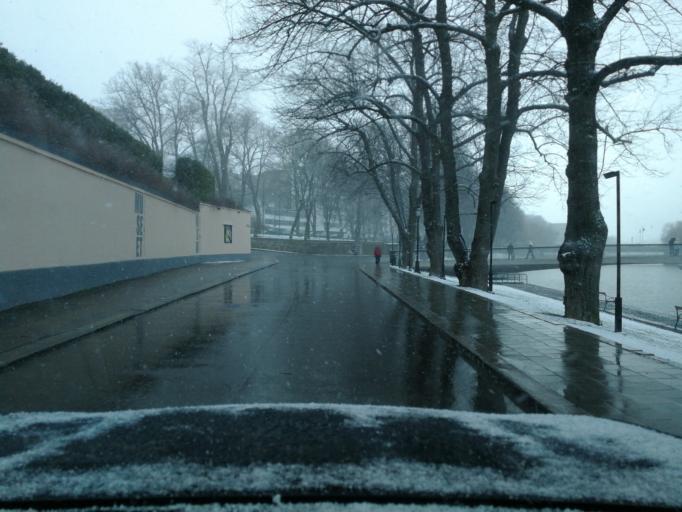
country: FI
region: Varsinais-Suomi
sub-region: Turku
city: Turku
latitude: 60.4498
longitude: 22.2731
